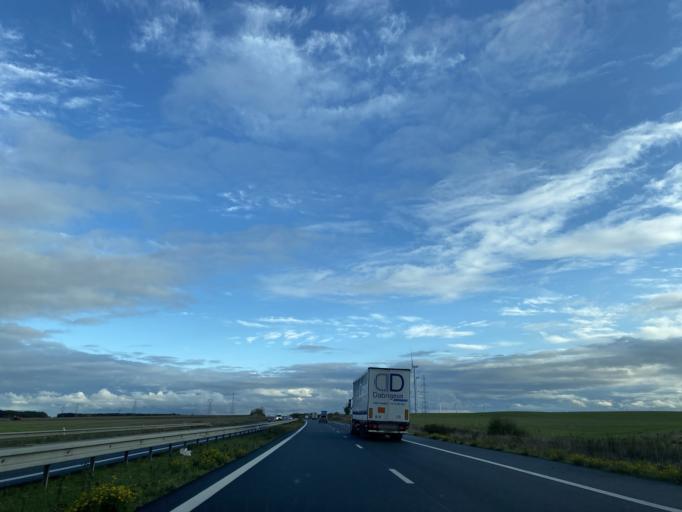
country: FR
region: Centre
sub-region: Departement du Cher
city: Mehun-sur-Yevre
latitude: 47.1079
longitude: 2.2085
